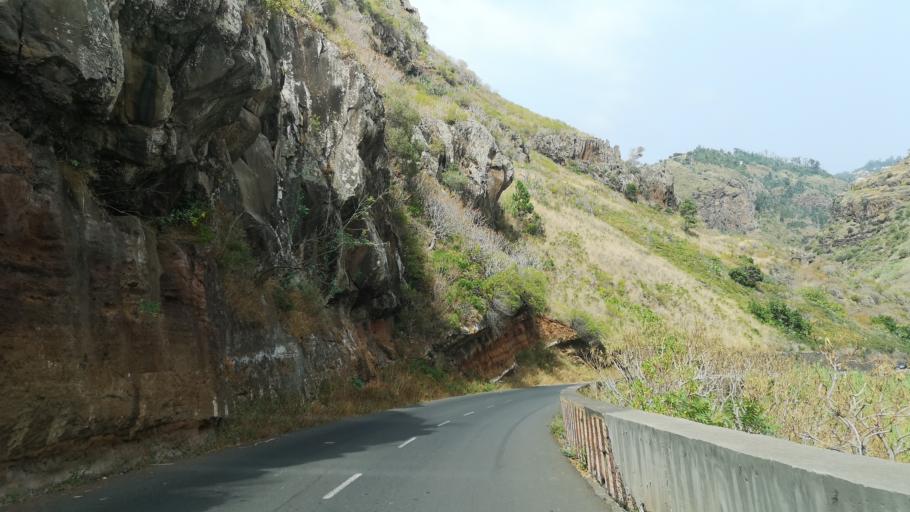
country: PT
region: Madeira
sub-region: Santa Cruz
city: Santa Cruz
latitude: 32.6607
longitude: -16.8118
